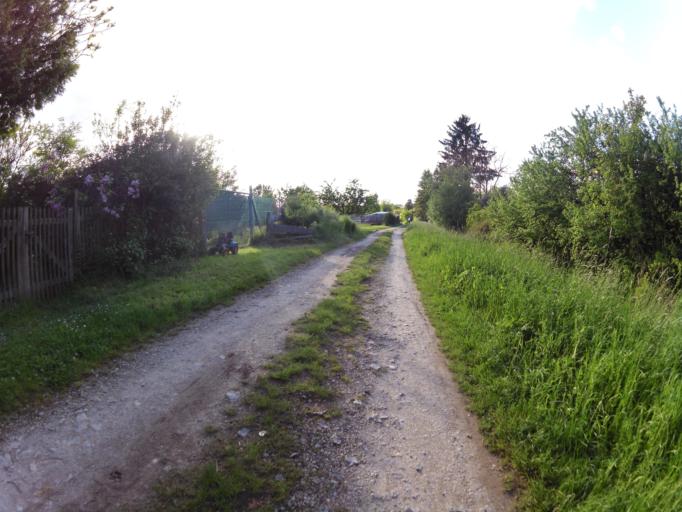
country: DE
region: Bavaria
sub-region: Regierungsbezirk Unterfranken
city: Volkach
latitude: 49.8680
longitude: 10.2177
